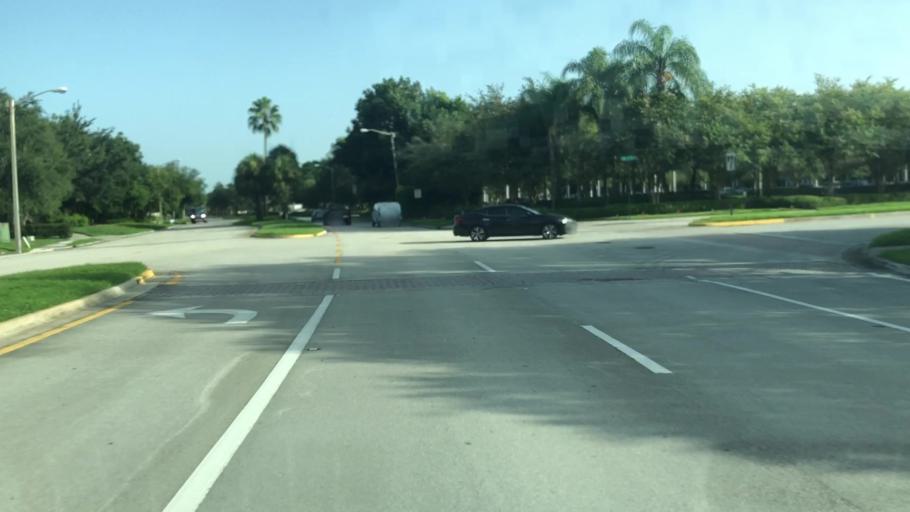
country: US
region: Florida
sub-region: Broward County
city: Pine Island Ridge
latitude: 26.1342
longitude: -80.3336
